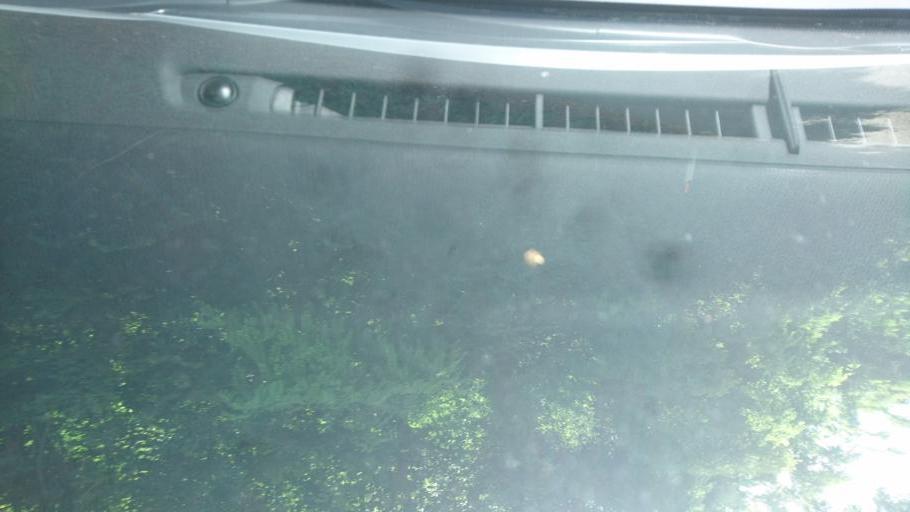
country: IT
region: Trentino-Alto Adige
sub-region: Provincia di Trento
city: Cavedine
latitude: 45.9723
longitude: 10.9698
